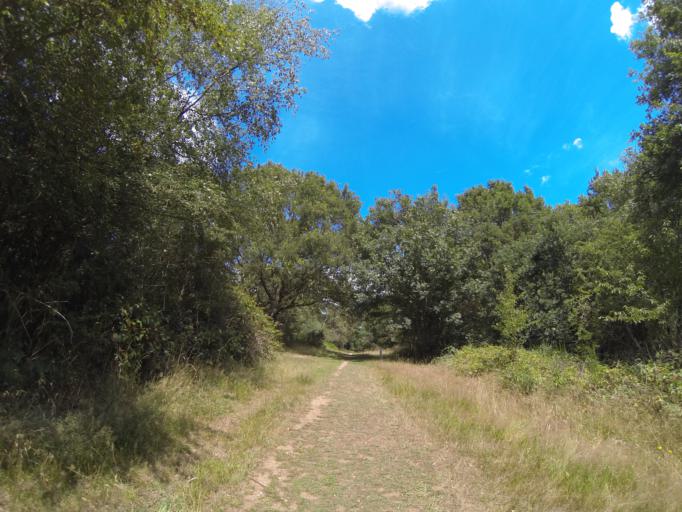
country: GB
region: England
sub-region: Kent
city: Swanley
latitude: 51.4313
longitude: 0.1827
